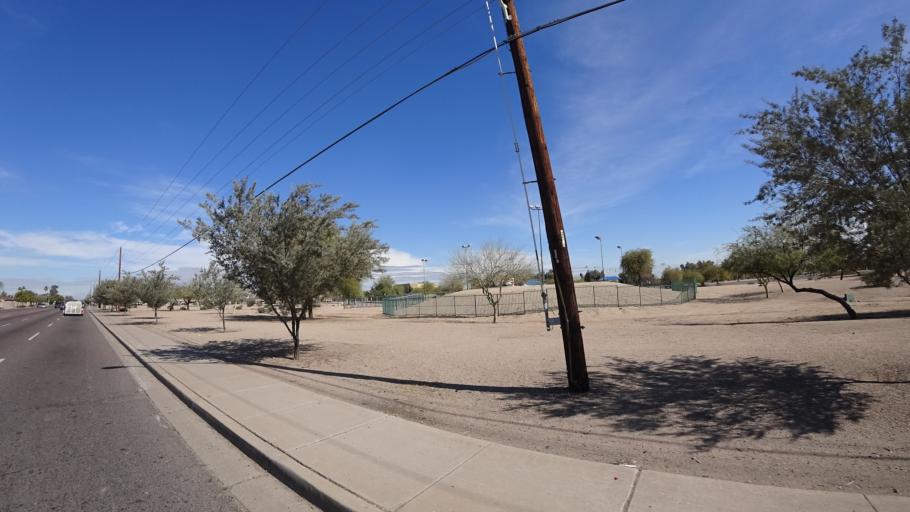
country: US
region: Arizona
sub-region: Maricopa County
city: Tolleson
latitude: 33.4741
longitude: -112.2032
